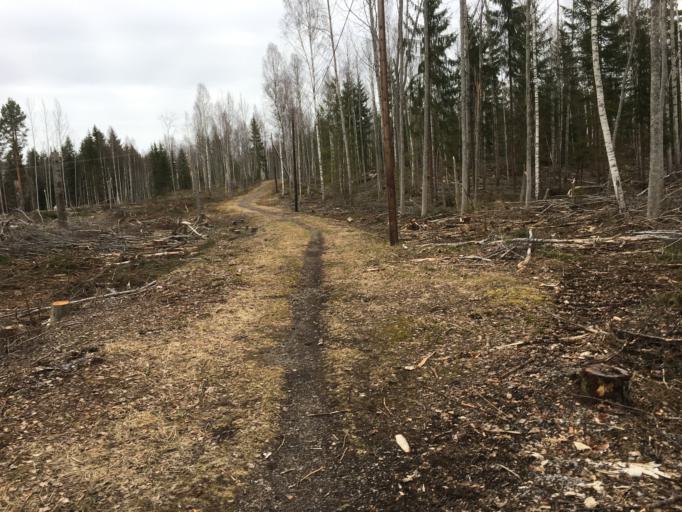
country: SE
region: Gaevleborg
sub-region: Hofors Kommun
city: Hofors
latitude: 60.5164
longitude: 16.4684
